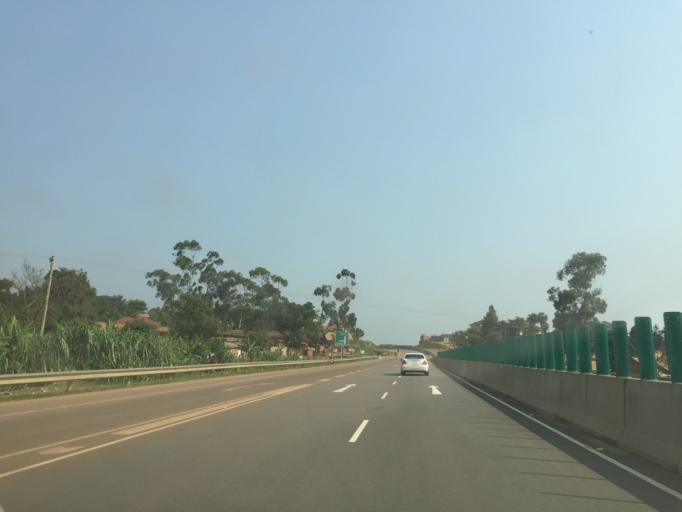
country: UG
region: Central Region
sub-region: Wakiso District
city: Kajansi
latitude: 0.2105
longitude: 32.5444
